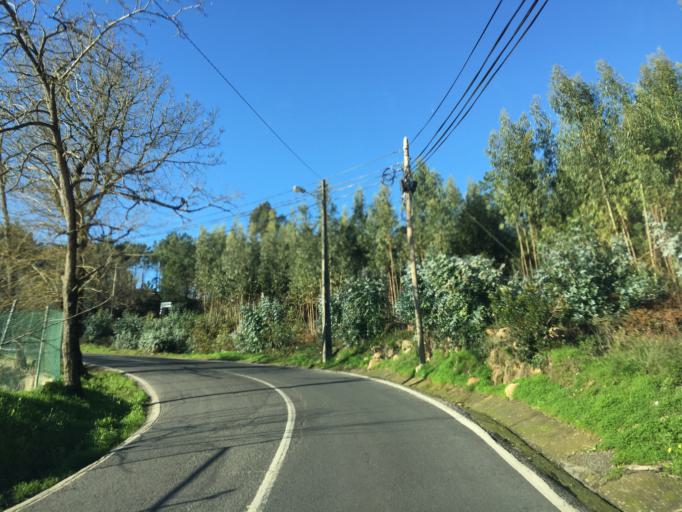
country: PT
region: Lisbon
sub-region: Odivelas
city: Canecas
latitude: 38.8191
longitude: -9.2318
